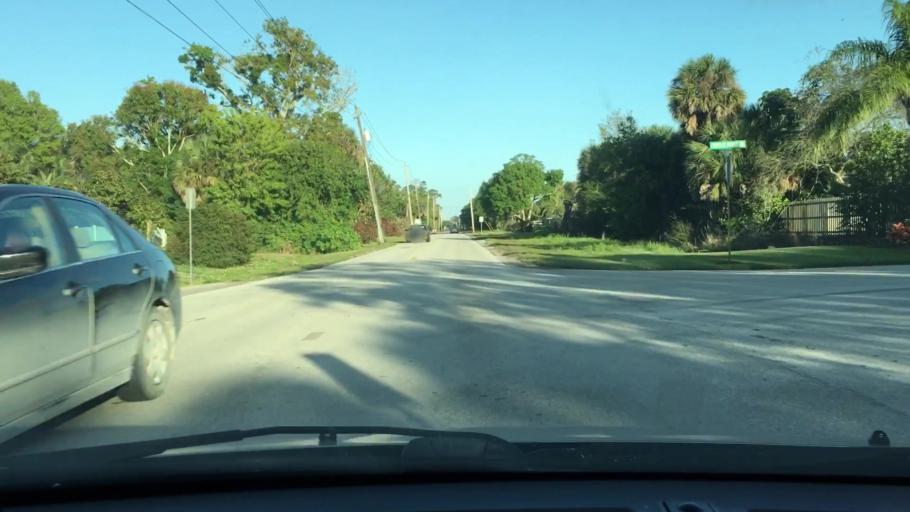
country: US
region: Florida
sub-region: Indian River County
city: Vero Beach South
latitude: 27.6461
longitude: -80.4399
